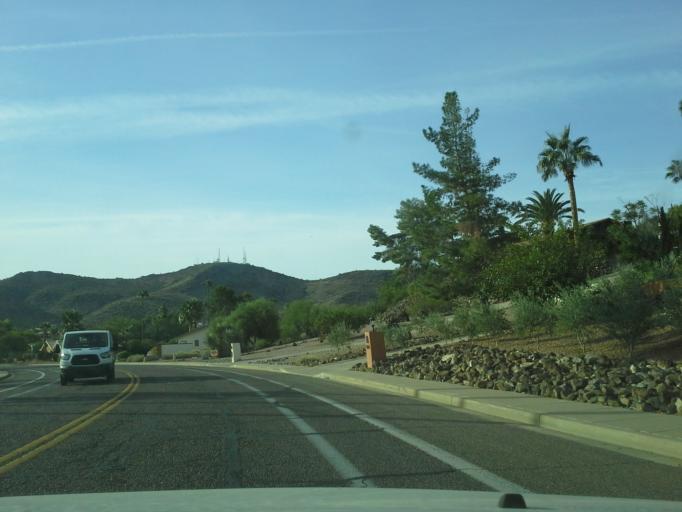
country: US
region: Arizona
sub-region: Maricopa County
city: Glendale
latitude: 33.6119
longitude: -112.0854
